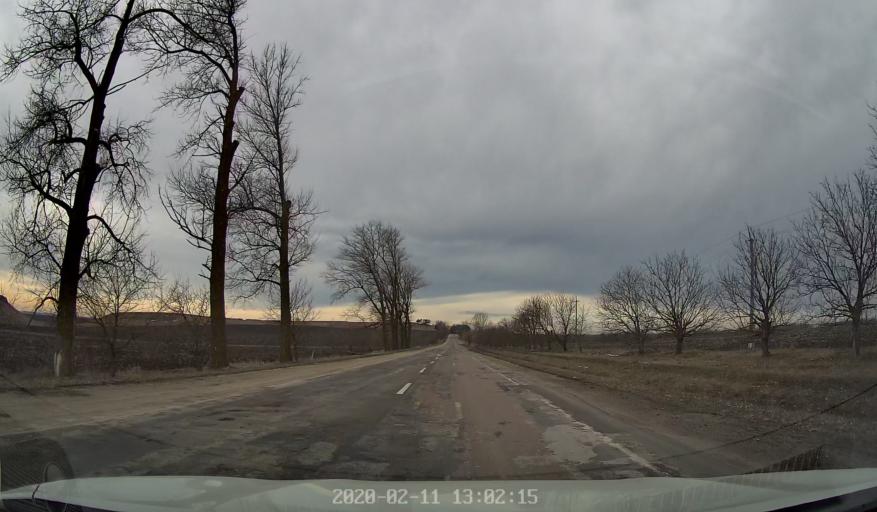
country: MD
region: Briceni
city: Briceni
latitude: 48.3164
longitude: 26.9849
